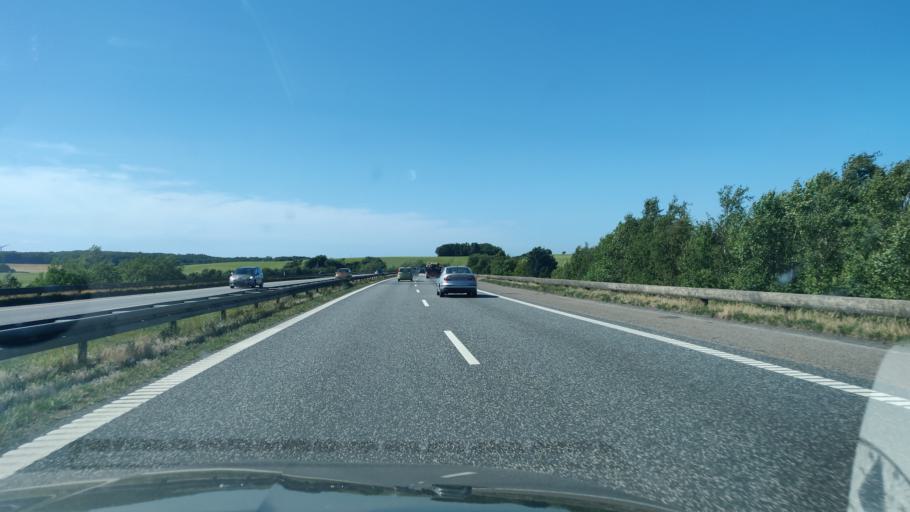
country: DK
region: Central Jutland
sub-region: Randers Kommune
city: Assentoft
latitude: 56.3895
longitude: 10.1036
